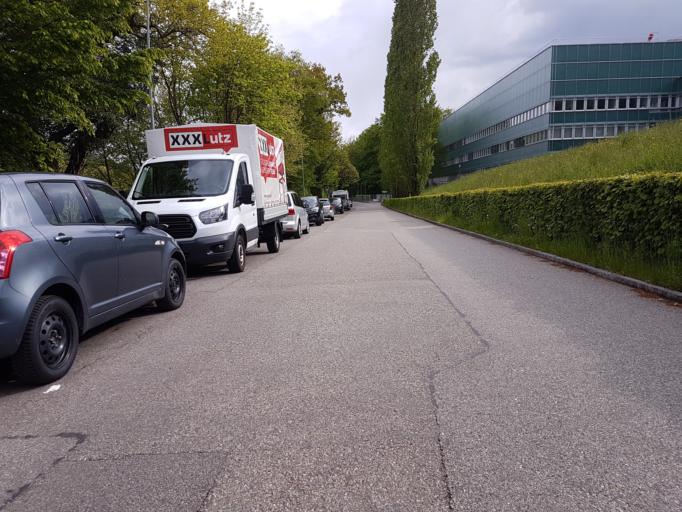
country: CH
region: Solothurn
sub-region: Bezirk Olten
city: Olten
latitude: 47.3574
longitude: 7.9062
